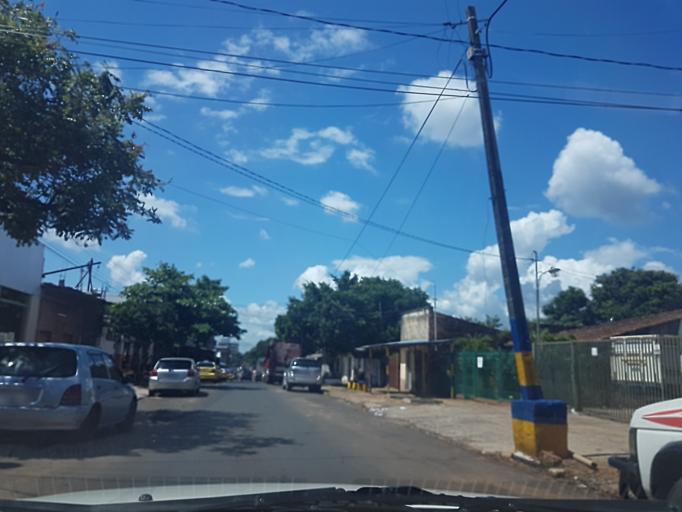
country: PY
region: Central
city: San Lorenzo
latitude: -25.2733
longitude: -57.4886
